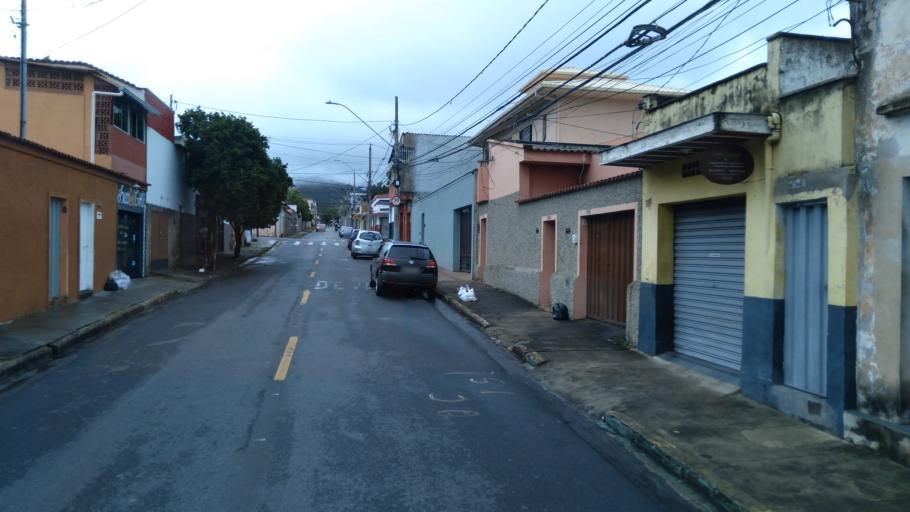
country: BR
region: Minas Gerais
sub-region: Belo Horizonte
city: Belo Horizonte
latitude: -19.9152
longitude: -43.9007
